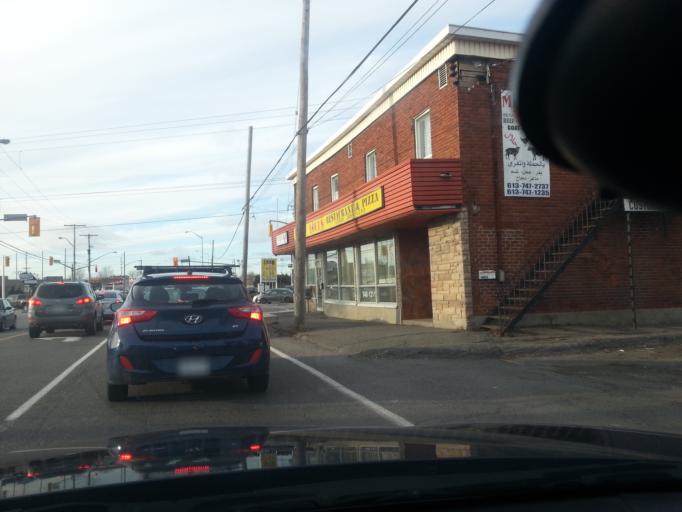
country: CA
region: Ontario
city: Ottawa
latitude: 45.4245
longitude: -75.6347
